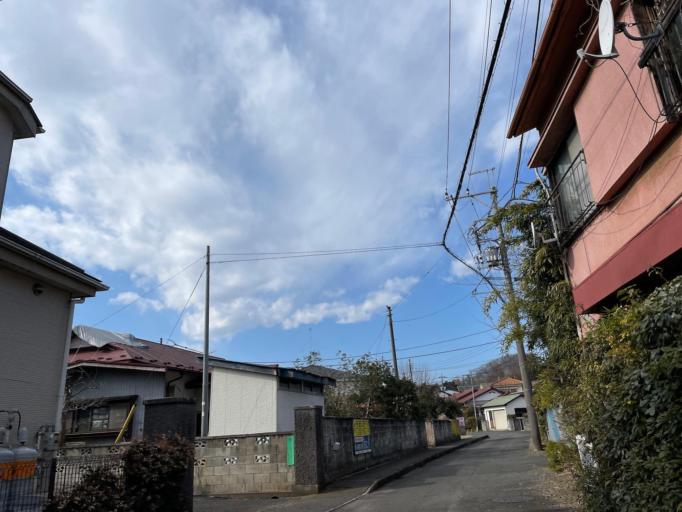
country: JP
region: Tokyo
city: Fussa
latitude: 35.7555
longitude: 139.3907
